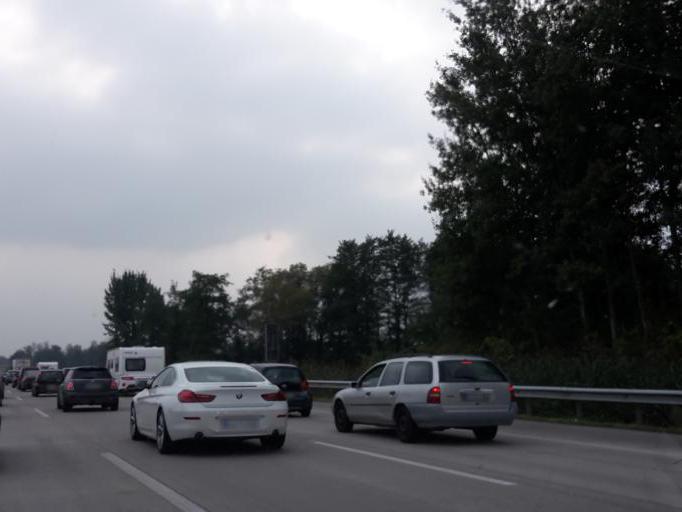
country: DE
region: Lower Saxony
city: Bakum
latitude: 52.7591
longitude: 8.1848
